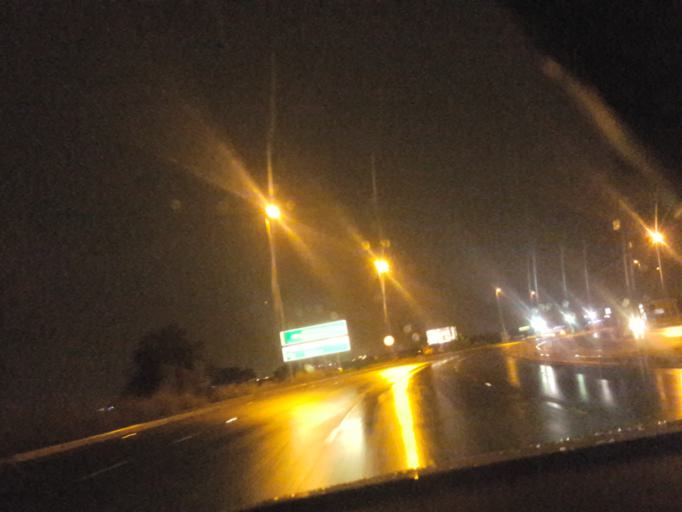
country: ZA
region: Gauteng
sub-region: City of Johannesburg Metropolitan Municipality
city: Diepsloot
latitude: -25.9860
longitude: 27.9842
